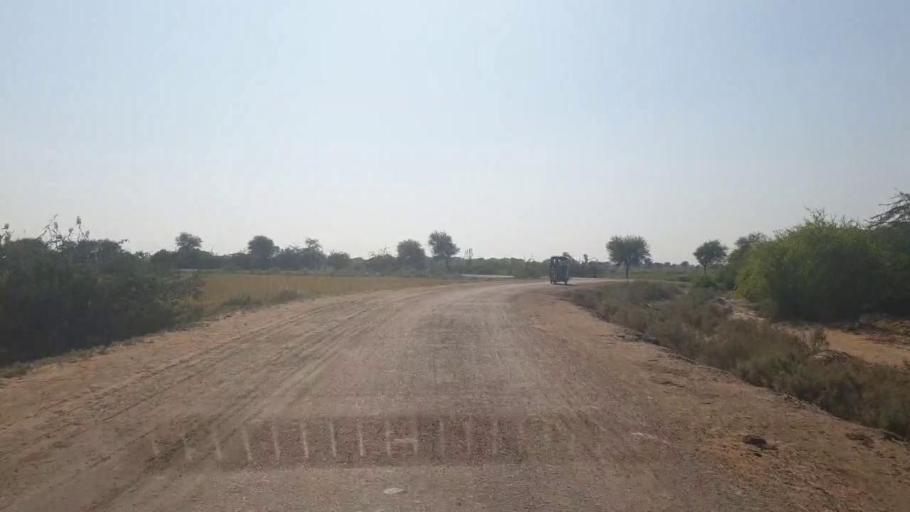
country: PK
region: Sindh
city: Badin
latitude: 24.5764
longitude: 68.8437
